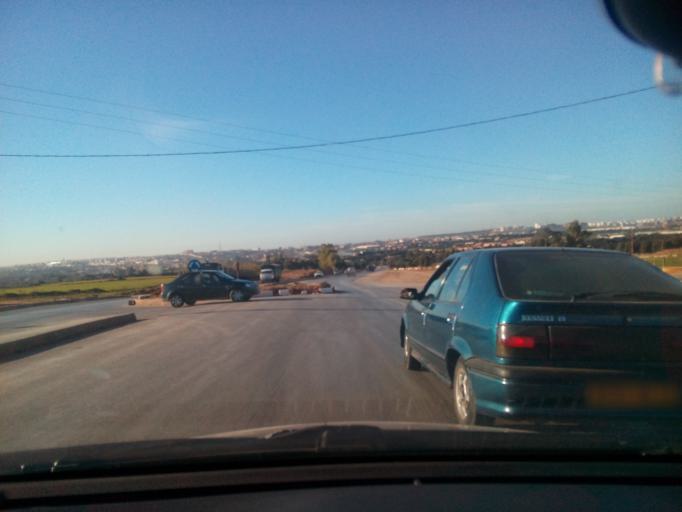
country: DZ
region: Mostaganem
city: Mostaganem
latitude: 35.9133
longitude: 0.1387
